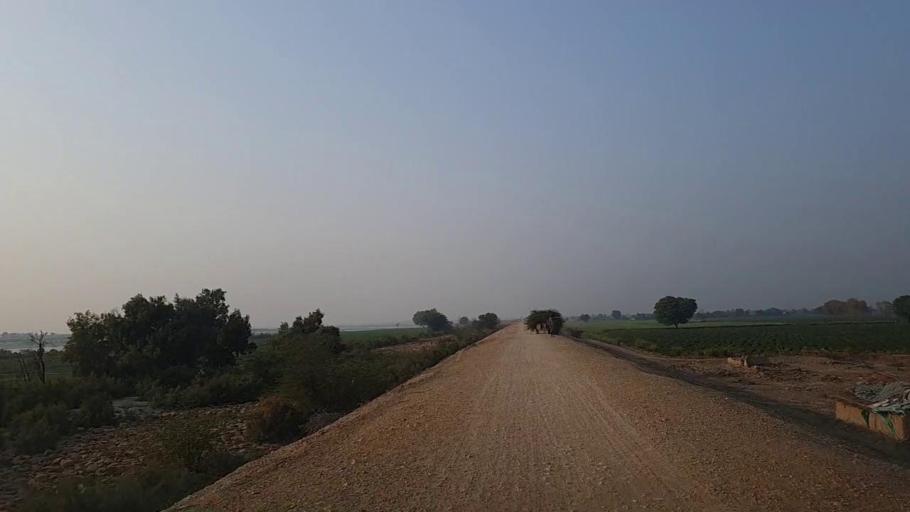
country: PK
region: Sindh
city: Sann
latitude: 26.1263
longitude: 68.1416
